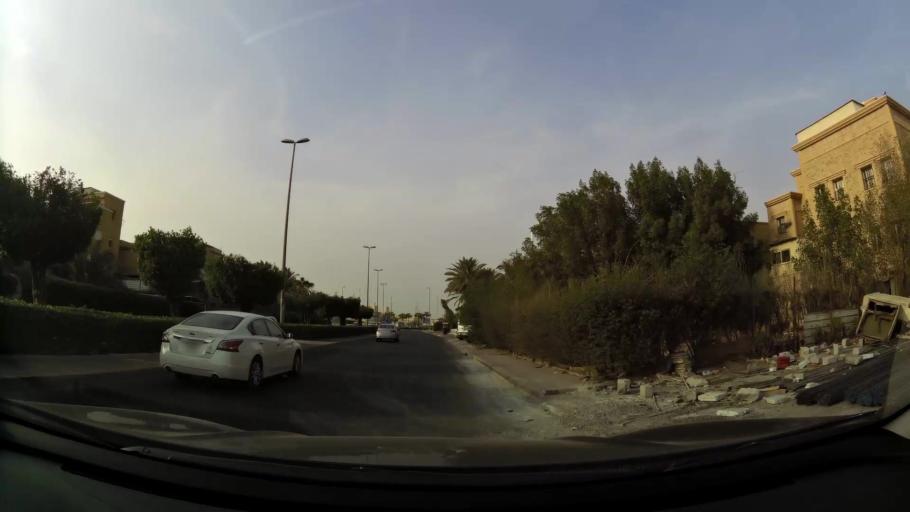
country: KW
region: Mubarak al Kabir
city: Mubarak al Kabir
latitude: 29.1998
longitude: 48.0791
